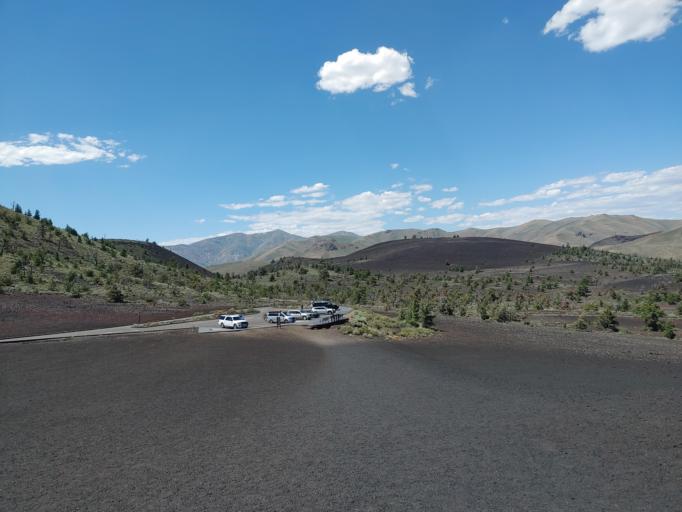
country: US
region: Idaho
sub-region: Butte County
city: Arco
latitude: 43.4446
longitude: -113.5545
